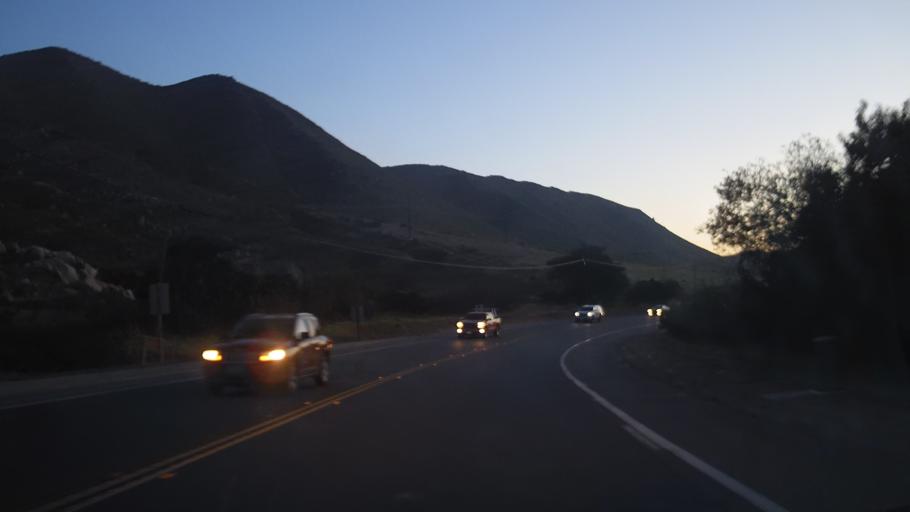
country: US
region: California
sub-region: San Diego County
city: Crest
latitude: 32.7798
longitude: -116.8664
